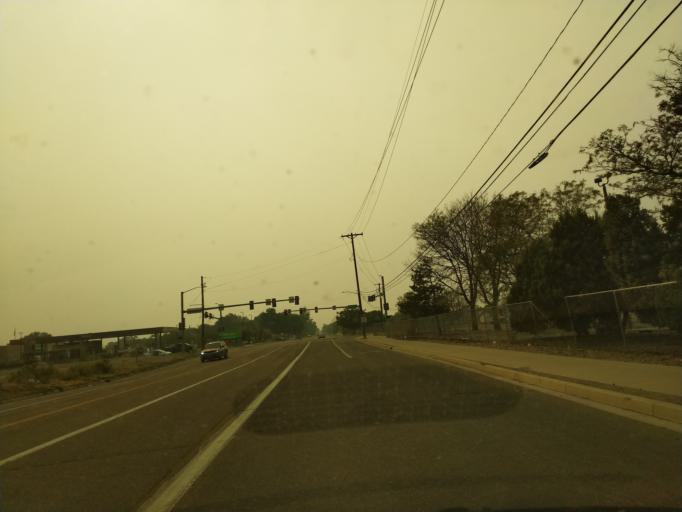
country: US
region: Colorado
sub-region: Mesa County
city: Clifton
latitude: 39.0846
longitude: -108.4720
